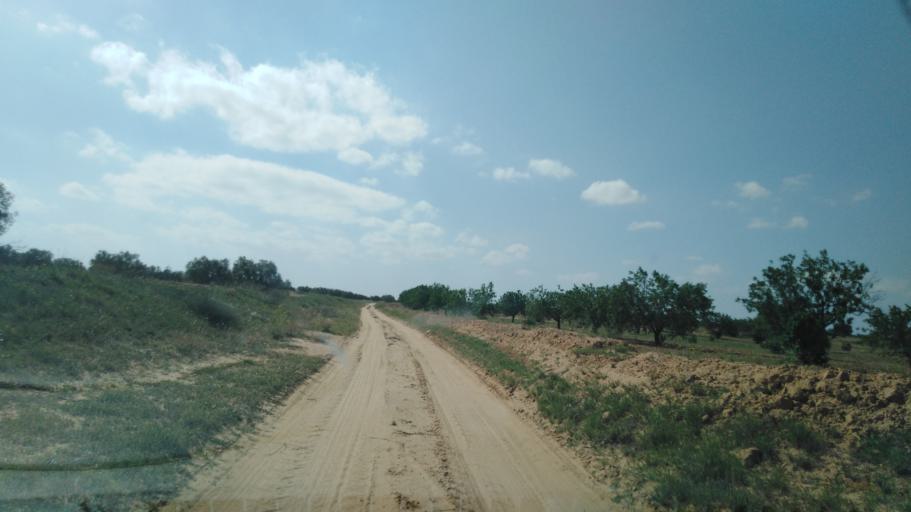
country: TN
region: Safaqis
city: Bi'r `Ali Bin Khalifah
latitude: 34.7911
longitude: 10.4032
